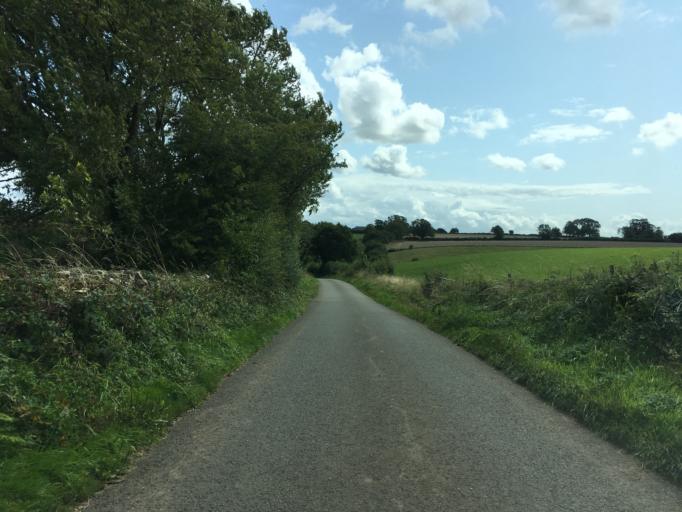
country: GB
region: England
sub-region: Wiltshire
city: Luckington
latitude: 51.6105
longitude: -2.2527
